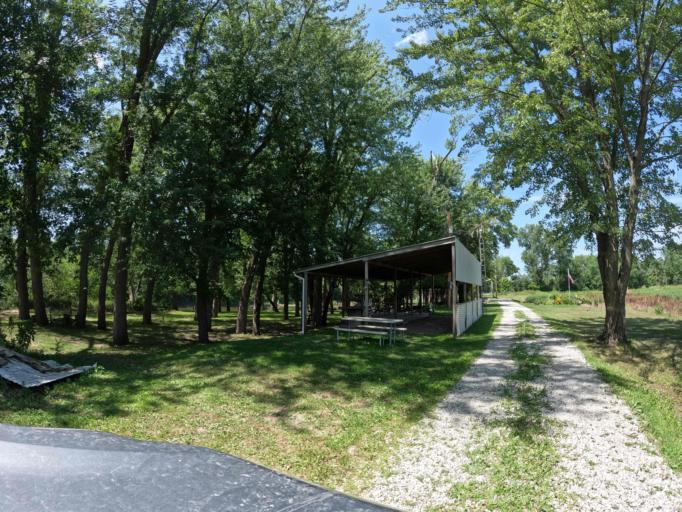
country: US
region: Iowa
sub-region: Henry County
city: Mount Pleasant
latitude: 40.8995
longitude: -91.5587
